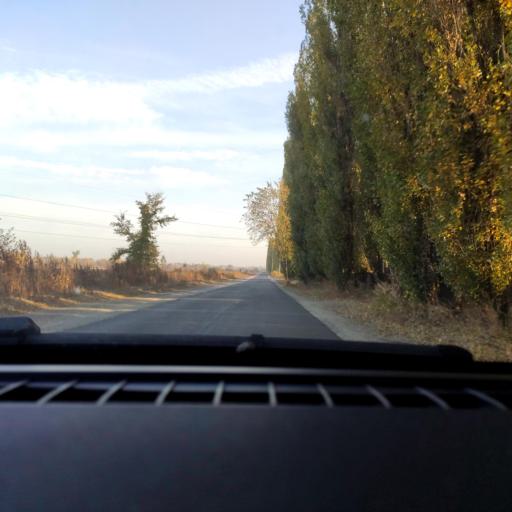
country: RU
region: Voronezj
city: Maslovka
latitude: 51.5222
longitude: 39.2262
